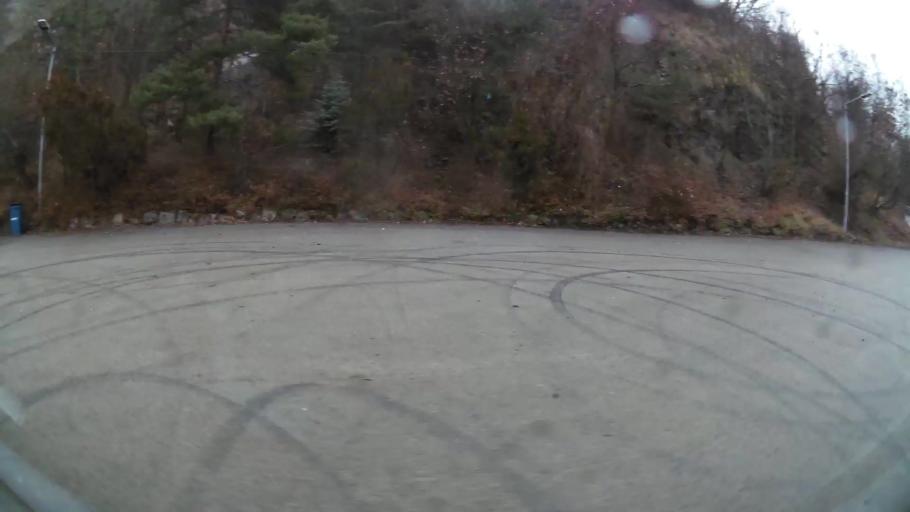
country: BG
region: Sofia-Capital
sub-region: Stolichna Obshtina
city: Sofia
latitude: 42.5934
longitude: 23.4224
